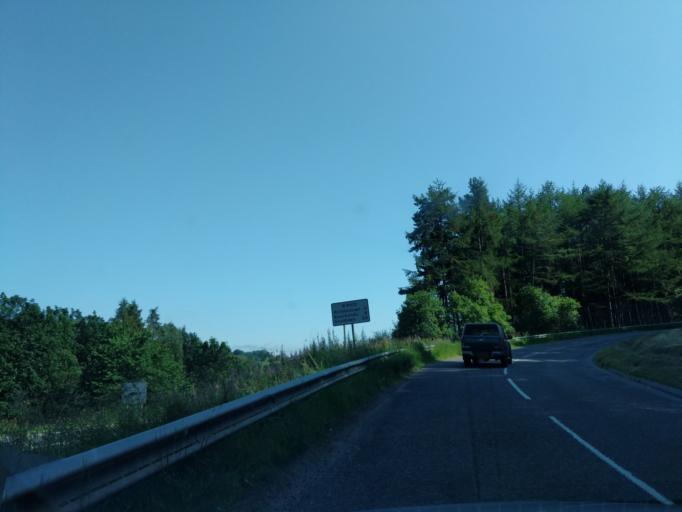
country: GB
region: Scotland
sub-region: Moray
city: Rothes
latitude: 57.4977
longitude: -3.1911
